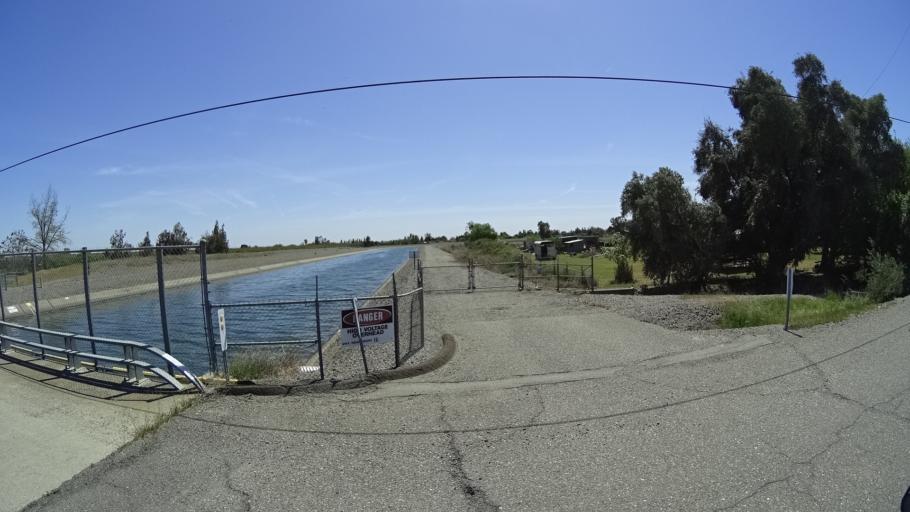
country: US
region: California
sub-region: Glenn County
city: Orland
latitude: 39.7398
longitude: -122.1546
